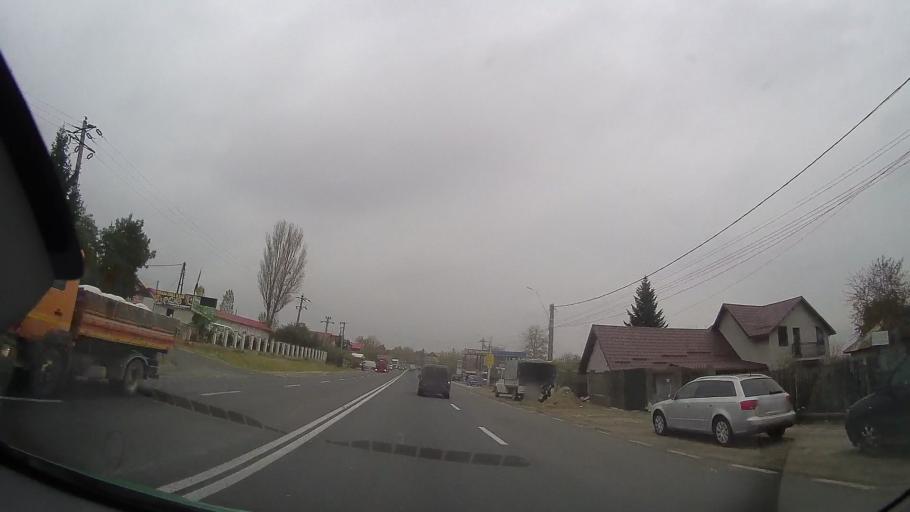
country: RO
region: Prahova
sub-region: Comuna Valea Calugareasca
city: Valea Calugareasca
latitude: 44.9622
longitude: 26.1551
